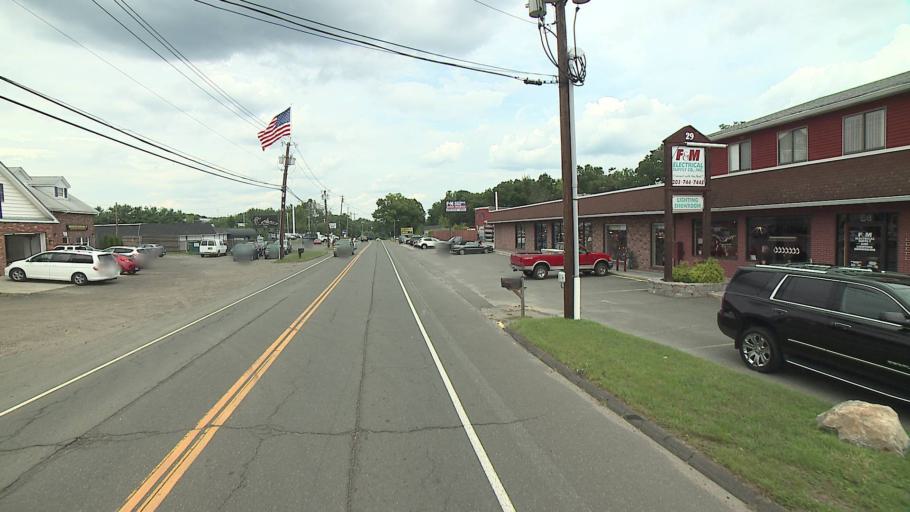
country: US
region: Connecticut
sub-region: Fairfield County
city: Danbury
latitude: 41.4082
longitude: -73.4292
